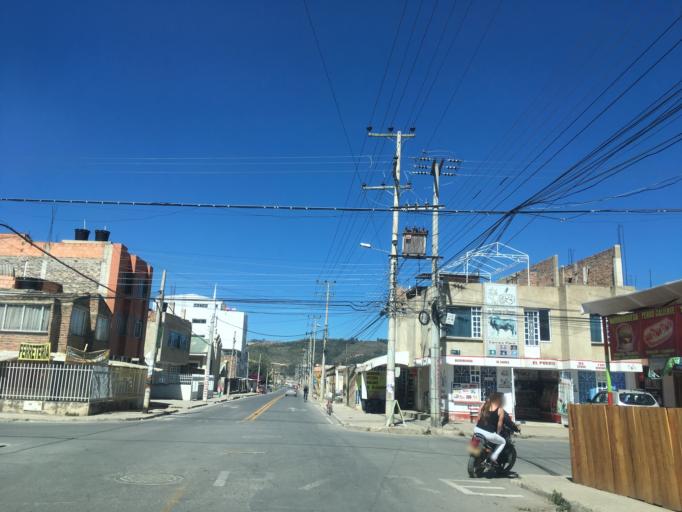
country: CO
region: Boyaca
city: Sogamoso
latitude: 5.7086
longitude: -72.9409
